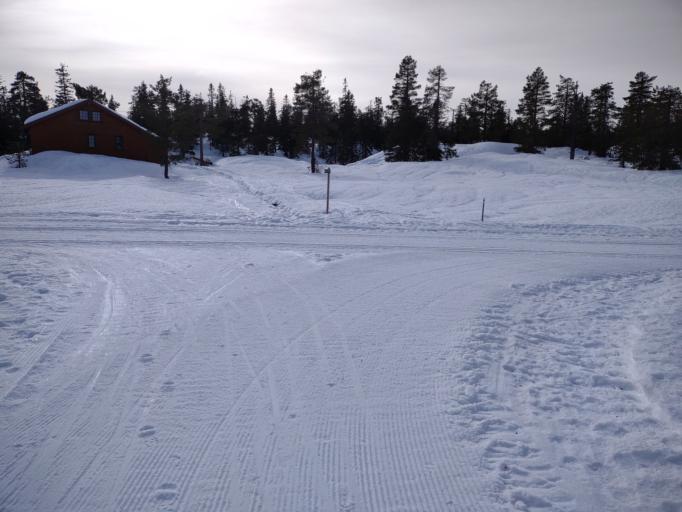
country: NO
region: Buskerud
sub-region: Flesberg
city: Lampeland
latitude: 59.7756
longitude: 9.4362
